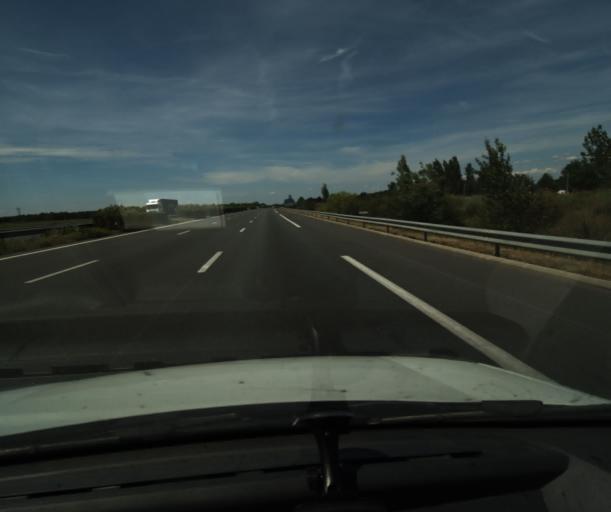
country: FR
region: Midi-Pyrenees
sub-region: Departement du Tarn-et-Garonne
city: Campsas
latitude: 43.8742
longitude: 1.3176
